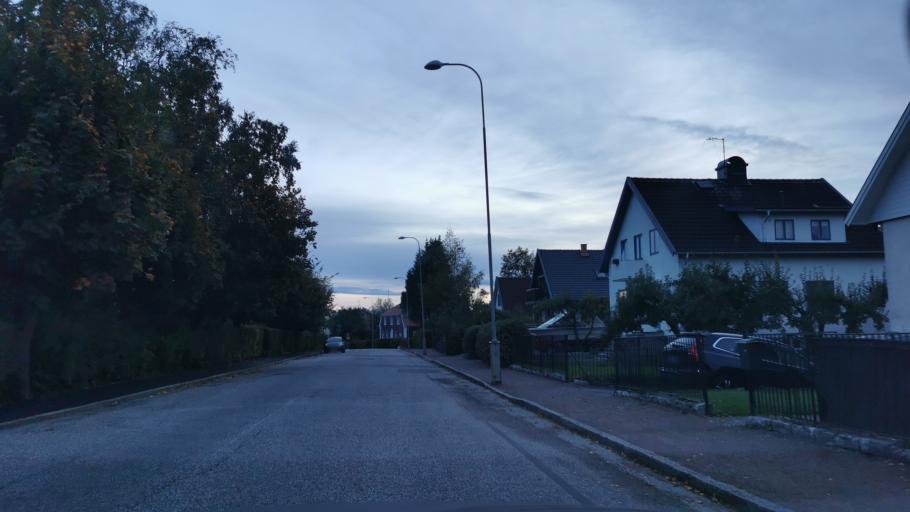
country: SE
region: Vaestra Goetaland
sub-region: Goteborg
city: Eriksbo
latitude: 57.7376
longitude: 12.0461
